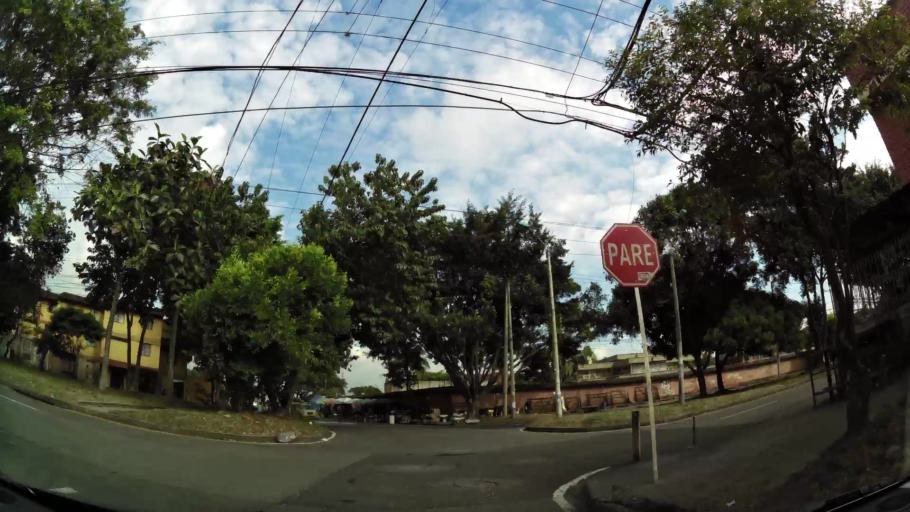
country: CO
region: Valle del Cauca
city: Cali
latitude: 3.4820
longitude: -76.4913
